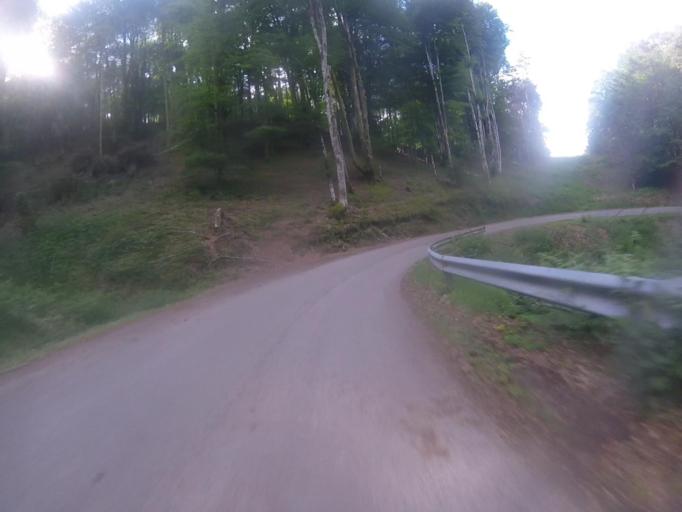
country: ES
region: Navarre
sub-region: Provincia de Navarra
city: Goizueta
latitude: 43.2326
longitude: -1.8059
